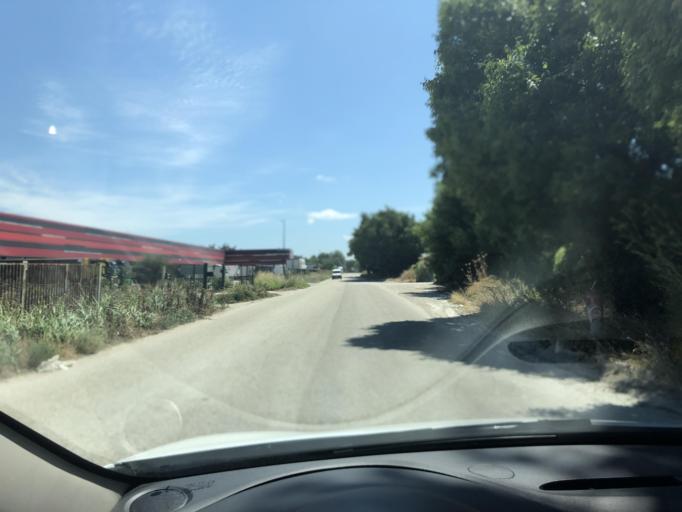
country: FR
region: Provence-Alpes-Cote d'Azur
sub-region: Departement des Bouches-du-Rhone
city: Chateaurenard
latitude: 43.9008
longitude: 4.8748
